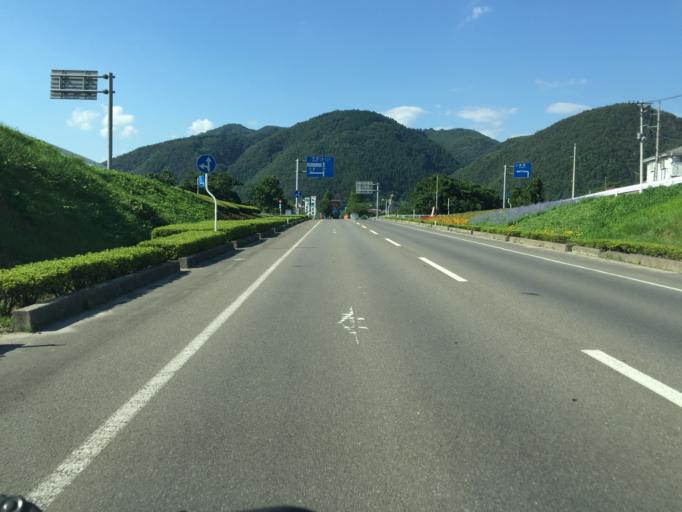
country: JP
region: Fukushima
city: Fukushima-shi
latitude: 37.8338
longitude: 140.4443
